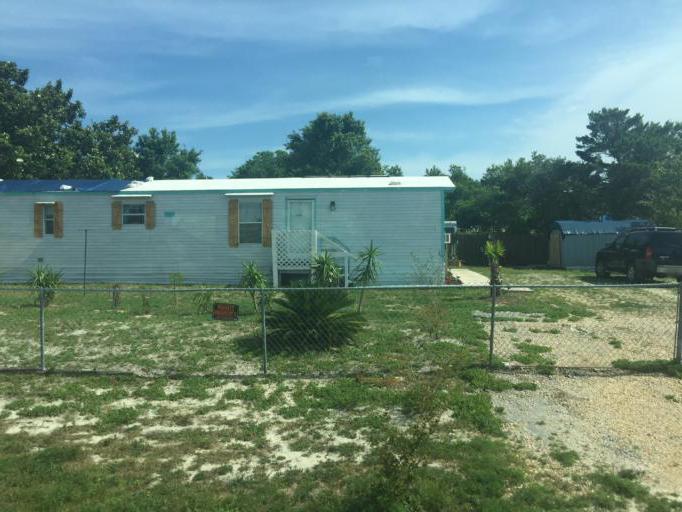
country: US
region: Florida
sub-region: Bay County
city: Laguna Beach
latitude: 30.2643
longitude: -85.9640
